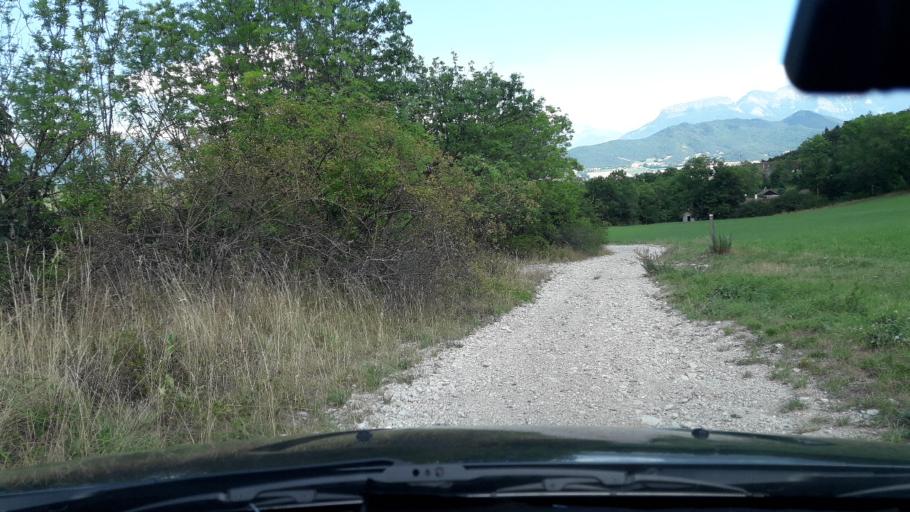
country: FR
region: Rhone-Alpes
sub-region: Departement de l'Isere
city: La Motte-Saint-Martin
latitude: 44.8614
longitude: 5.5987
